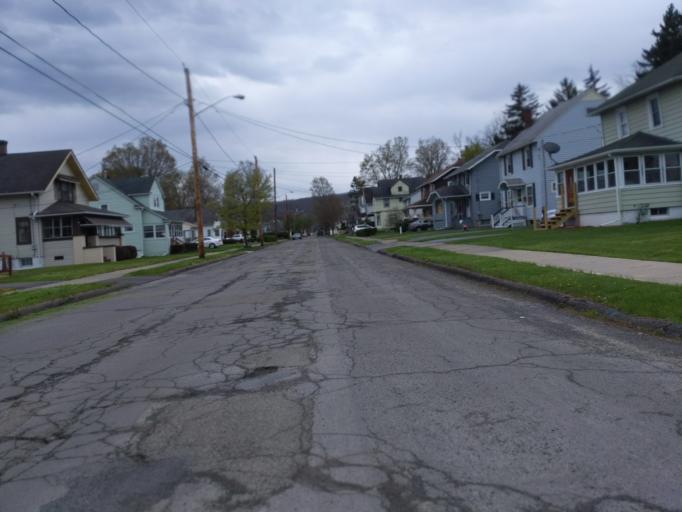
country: US
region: New York
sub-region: Chemung County
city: Southport
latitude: 42.0676
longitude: -76.8135
